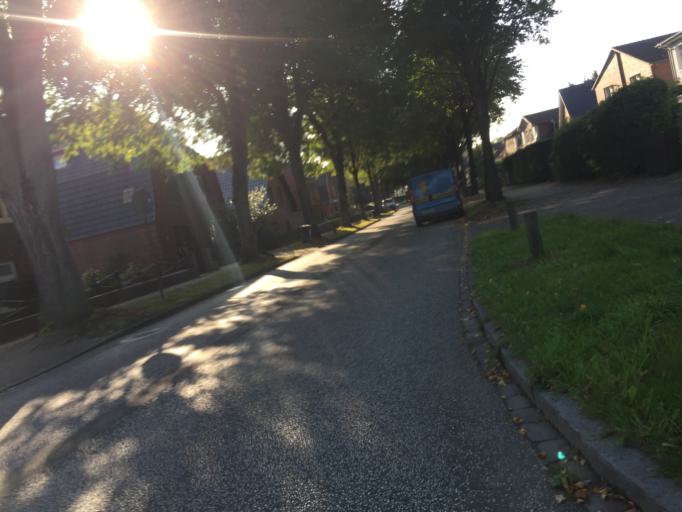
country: DE
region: Schleswig-Holstein
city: Oelixdorf
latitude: 53.9278
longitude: 9.5428
